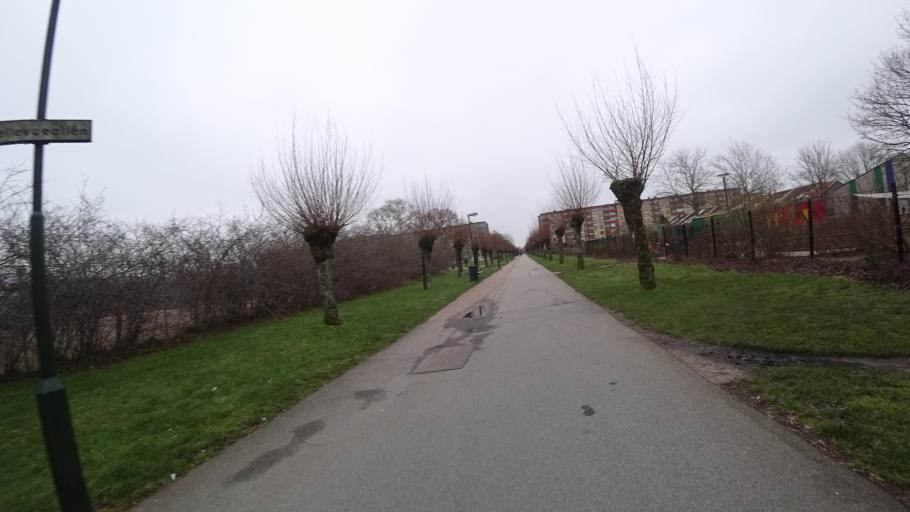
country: SE
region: Skane
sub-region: Malmo
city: Malmoe
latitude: 55.5831
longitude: 12.9720
